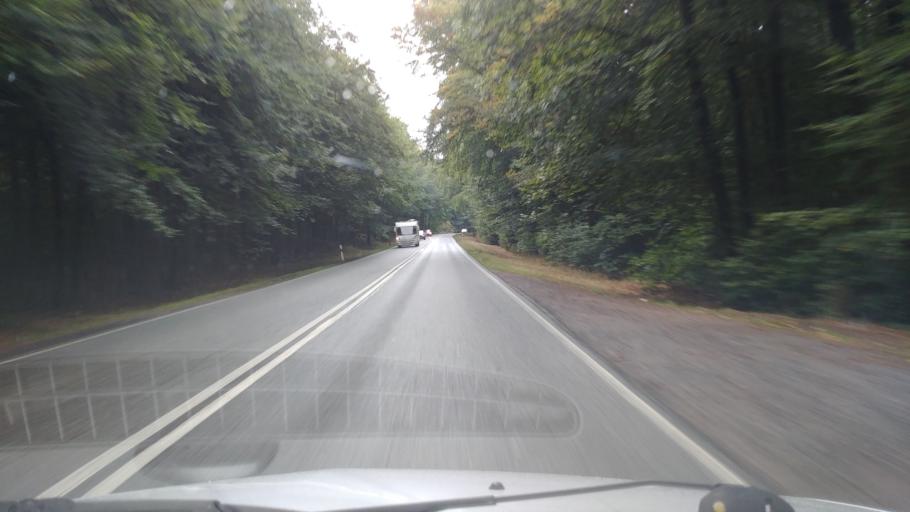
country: DE
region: Rheinland-Pfalz
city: Wahlenau
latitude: 49.9123
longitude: 7.2342
